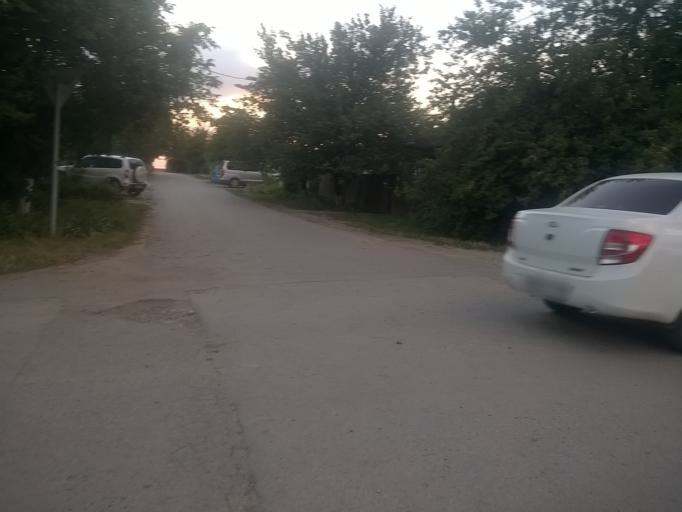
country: RU
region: Rostov
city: Donetsk
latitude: 48.3334
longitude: 39.9549
